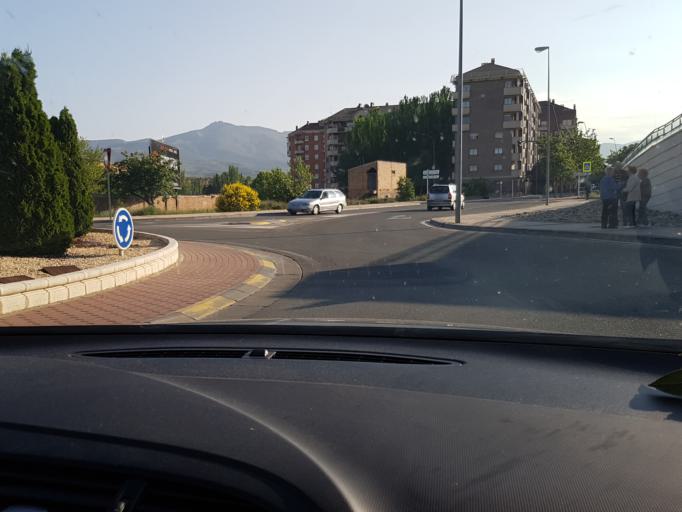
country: ES
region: La Rioja
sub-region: Provincia de La Rioja
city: Arnedo
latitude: 42.2275
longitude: -2.0940
